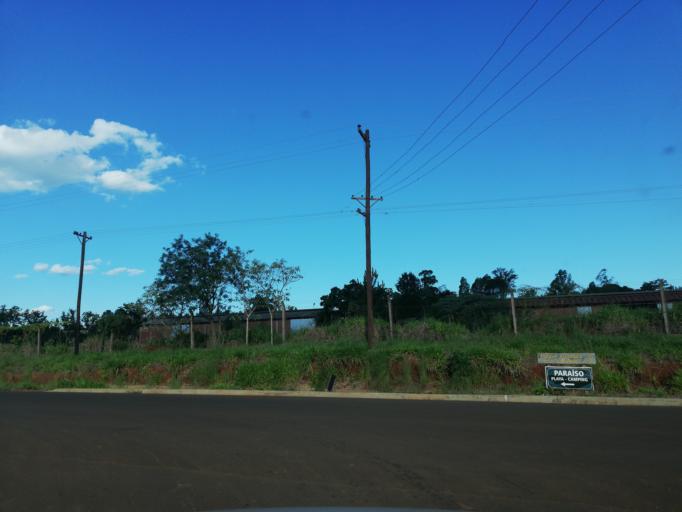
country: AR
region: Misiones
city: Garupa
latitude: -27.4648
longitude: -55.7976
